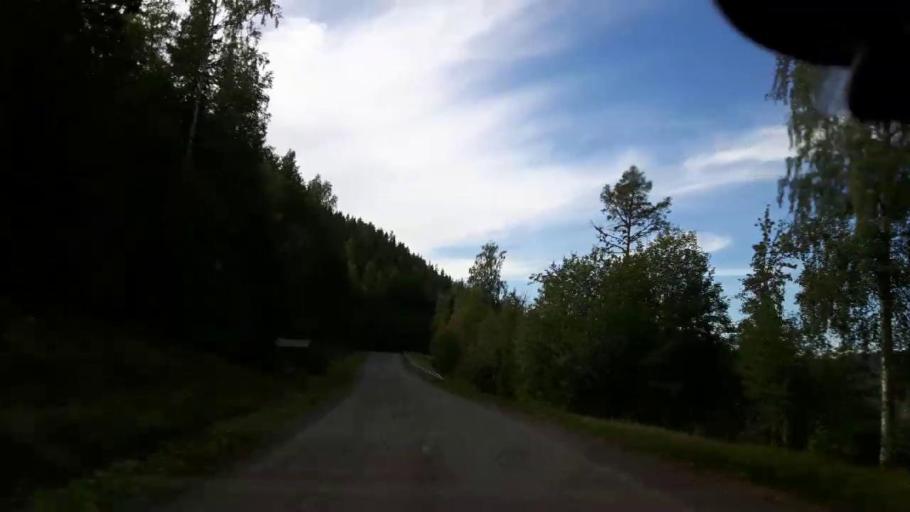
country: SE
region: Jaemtland
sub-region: Ragunda Kommun
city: Hammarstrand
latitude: 63.1374
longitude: 16.1787
